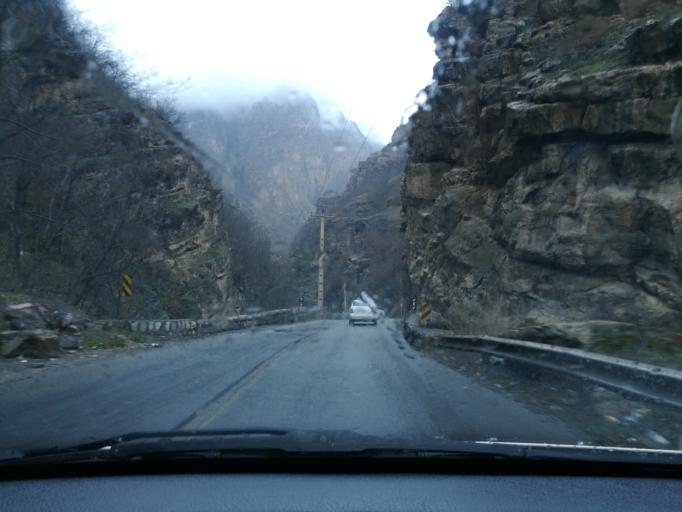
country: IR
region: Mazandaran
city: Chalus
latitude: 36.2686
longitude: 51.2521
